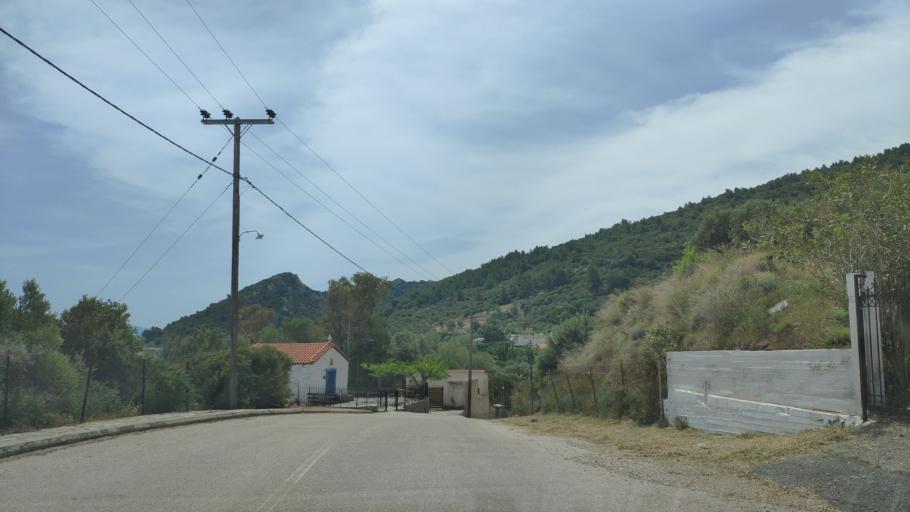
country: GR
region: Attica
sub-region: Nomarchia Anatolikis Attikis
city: Grammatiko
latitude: 38.2643
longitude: 23.9751
